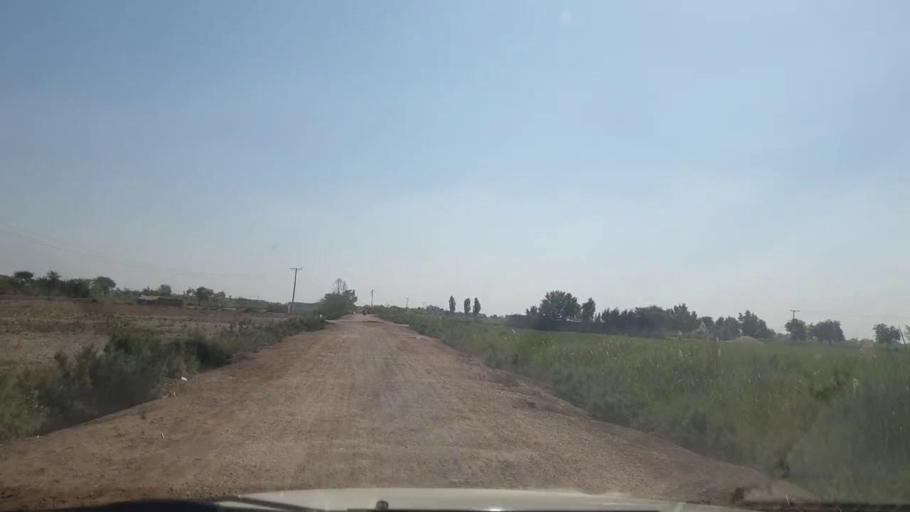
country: PK
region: Sindh
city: Mirpur Khas
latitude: 25.5107
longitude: 69.0843
